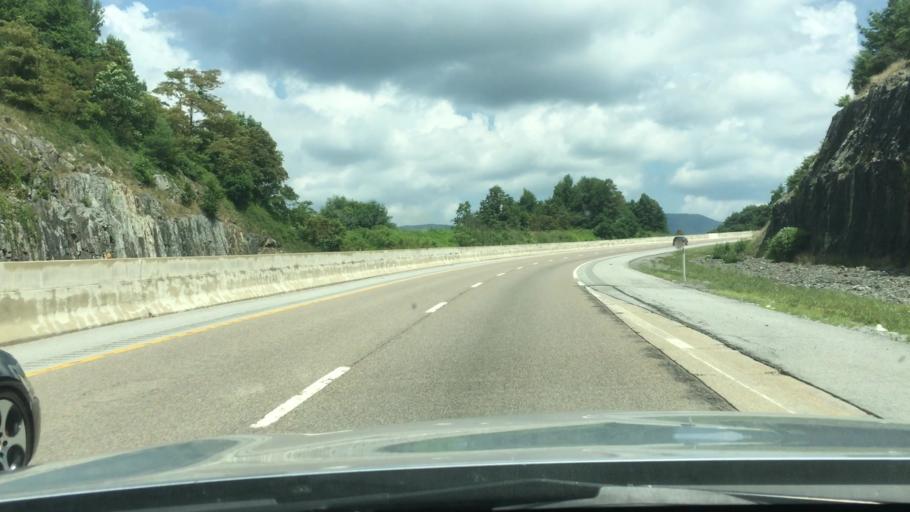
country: US
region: Tennessee
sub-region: Unicoi County
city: Banner Hill
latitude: 36.0163
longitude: -82.5480
